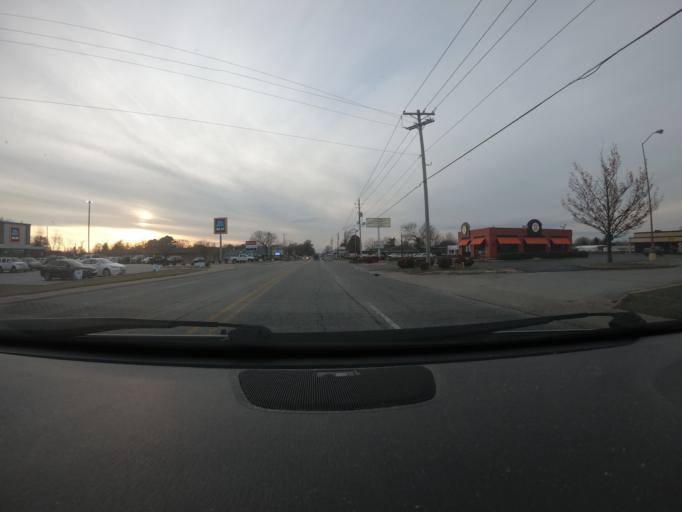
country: US
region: Arkansas
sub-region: Benton County
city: Rogers
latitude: 36.3338
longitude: -94.1355
